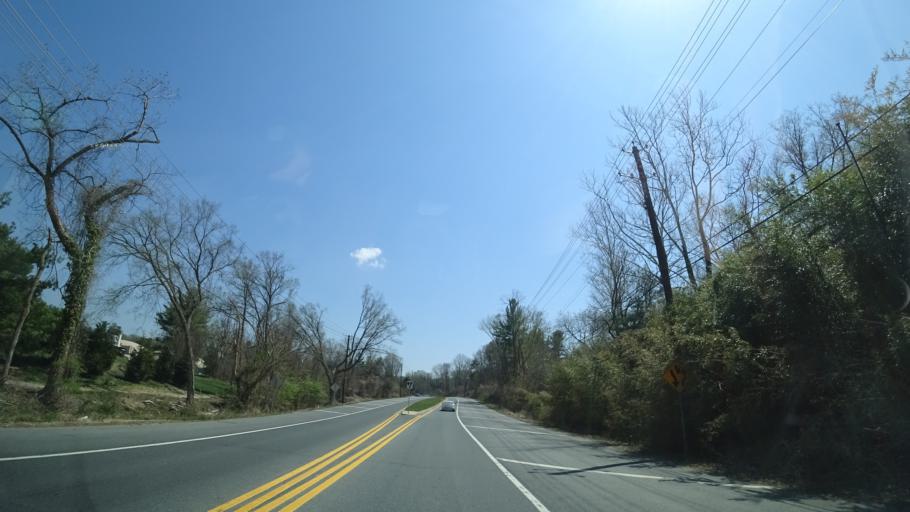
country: US
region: Maryland
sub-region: Montgomery County
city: Cabin John
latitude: 39.0115
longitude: -77.1553
